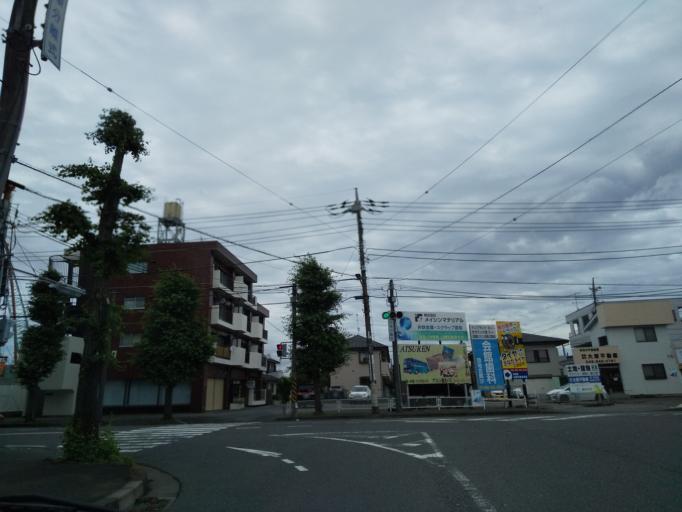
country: JP
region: Kanagawa
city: Zama
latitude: 35.5106
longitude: 139.3578
